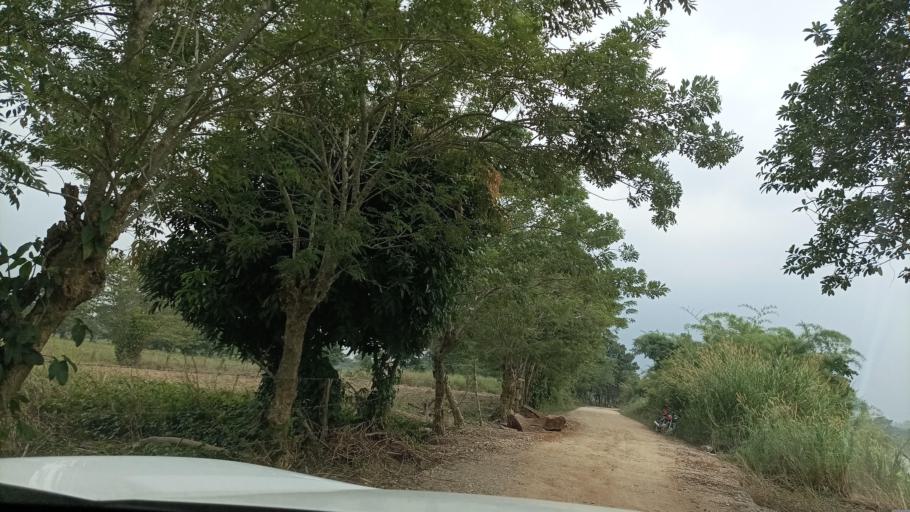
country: MX
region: Veracruz
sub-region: Moloacan
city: Cuichapa
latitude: 17.5835
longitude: -94.2146
